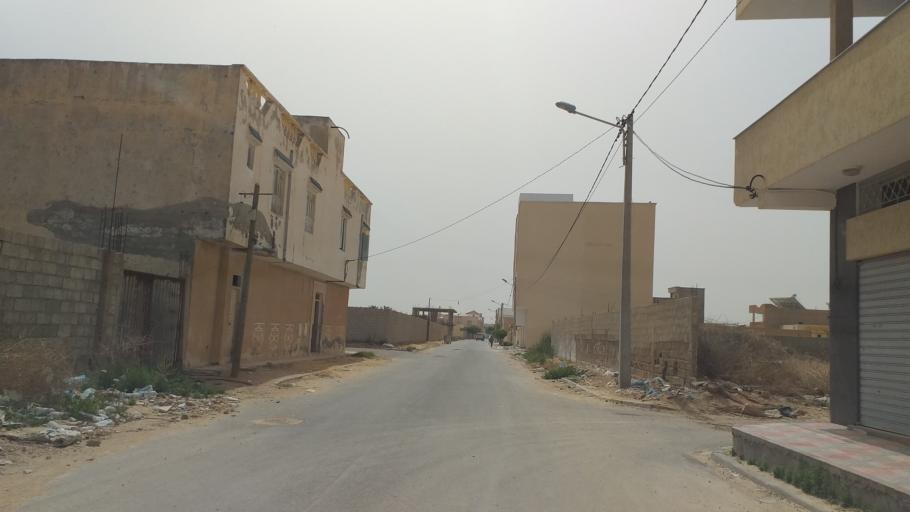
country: TN
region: Qabis
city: Gabes
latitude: 33.9435
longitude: 10.0567
